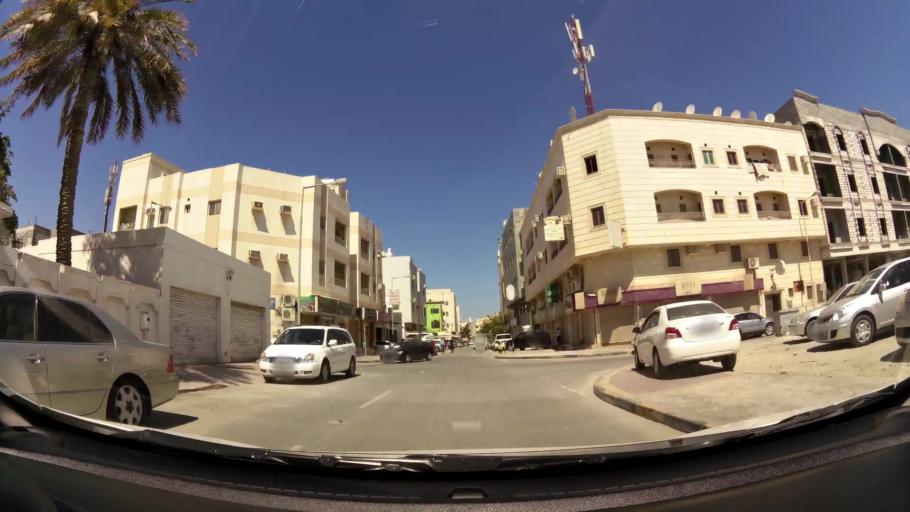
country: BH
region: Muharraq
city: Al Muharraq
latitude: 26.2642
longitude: 50.6077
